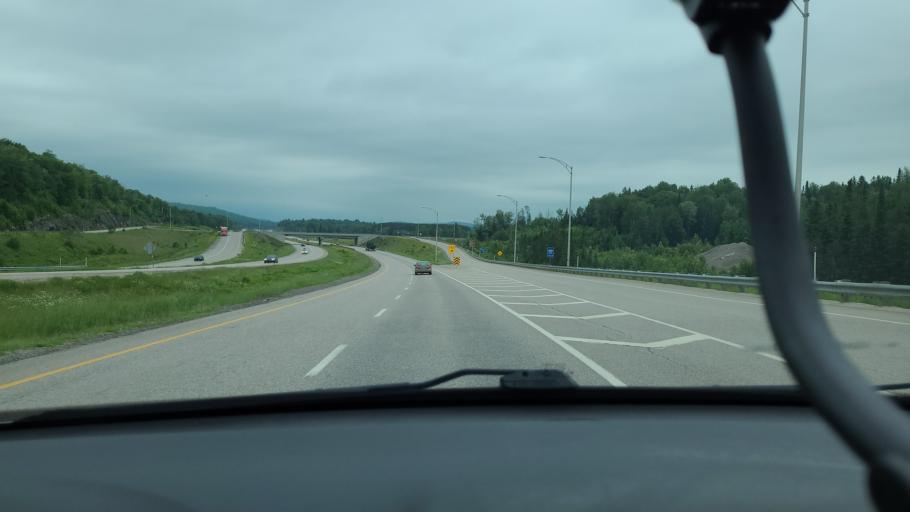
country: CA
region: Quebec
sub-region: Laurentides
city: Labelle
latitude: 46.2737
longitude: -74.7393
